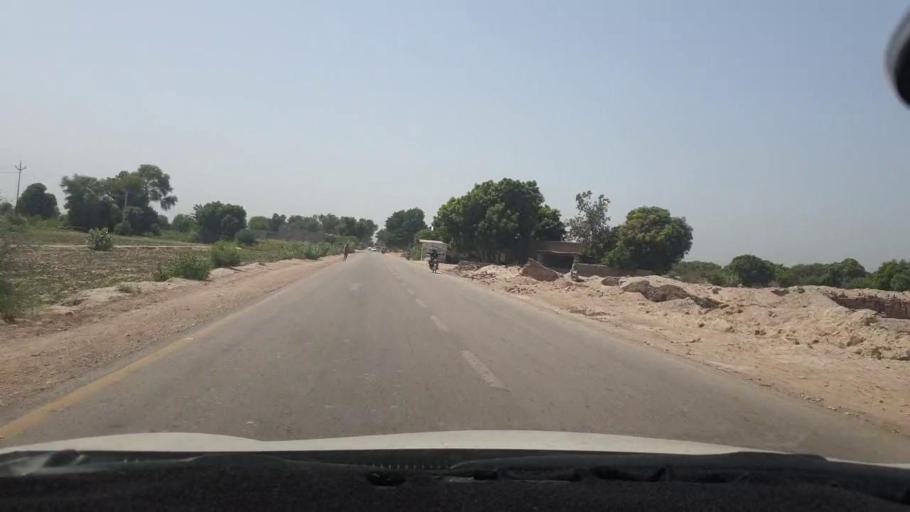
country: PK
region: Sindh
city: Bhit Shah
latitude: 25.8539
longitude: 68.4953
